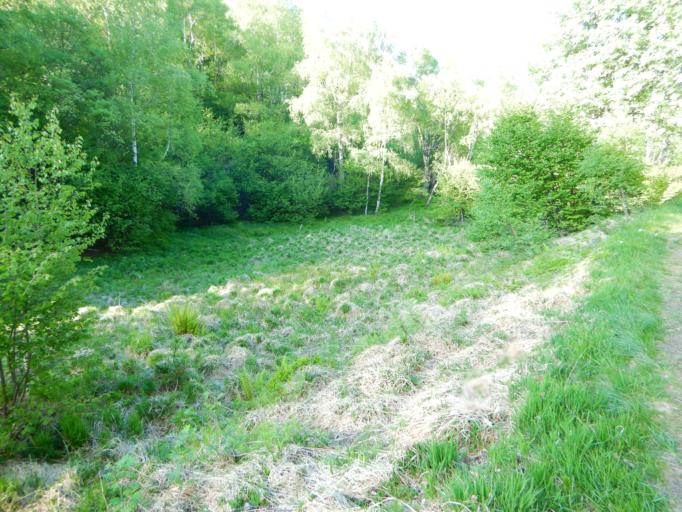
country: CH
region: Ticino
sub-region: Bellinzona District
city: Cadenazzo
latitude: 46.1305
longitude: 8.9549
